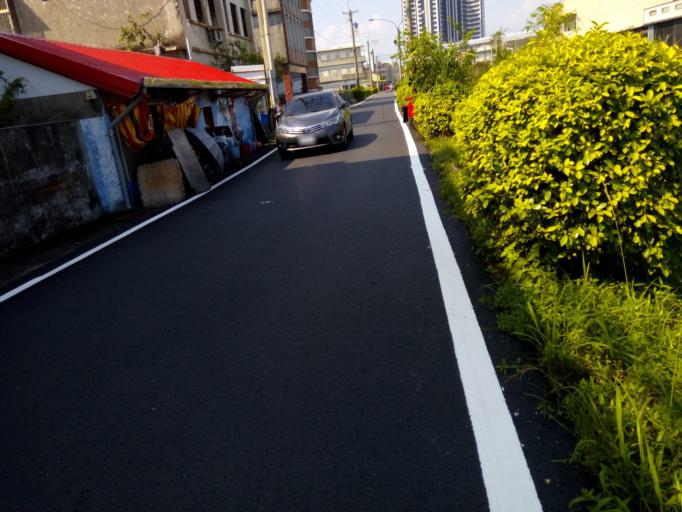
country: TW
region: Taiwan
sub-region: Yilan
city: Yilan
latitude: 24.6716
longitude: 121.7803
